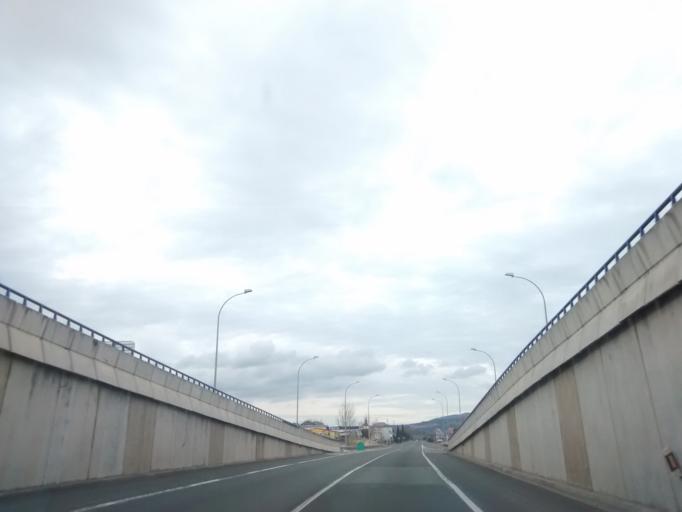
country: ES
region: La Rioja
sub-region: Provincia de La Rioja
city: Haro
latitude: 42.5637
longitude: -2.8391
